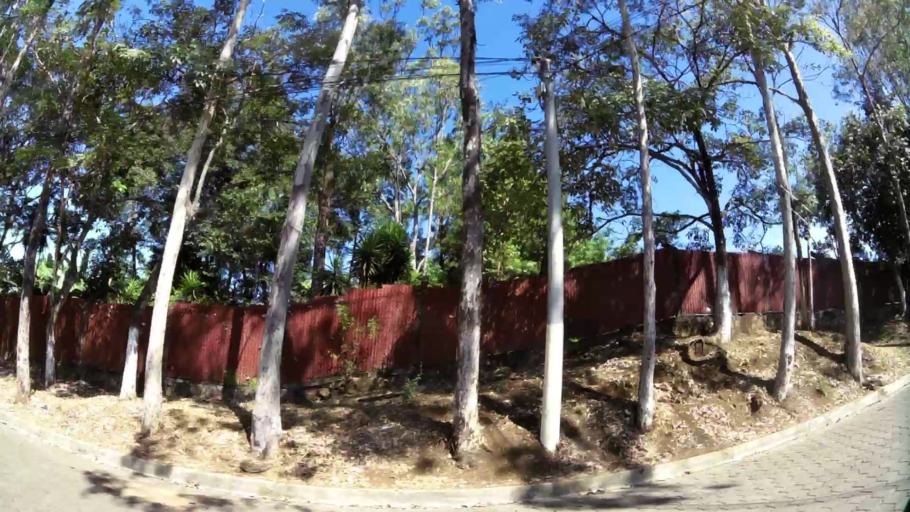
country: SV
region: Ahuachapan
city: Ahuachapan
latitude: 13.9227
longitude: -89.8430
